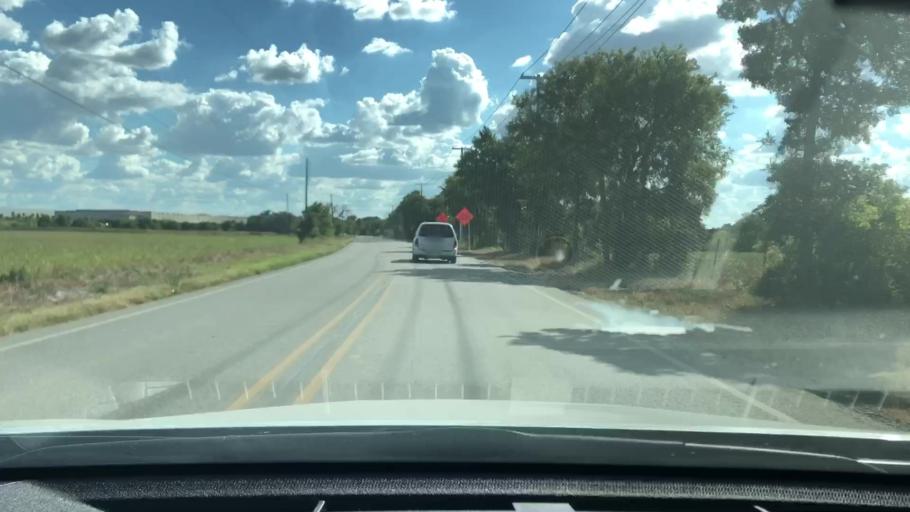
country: US
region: Texas
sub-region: Guadalupe County
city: Northcliff
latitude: 29.6536
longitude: -98.2124
